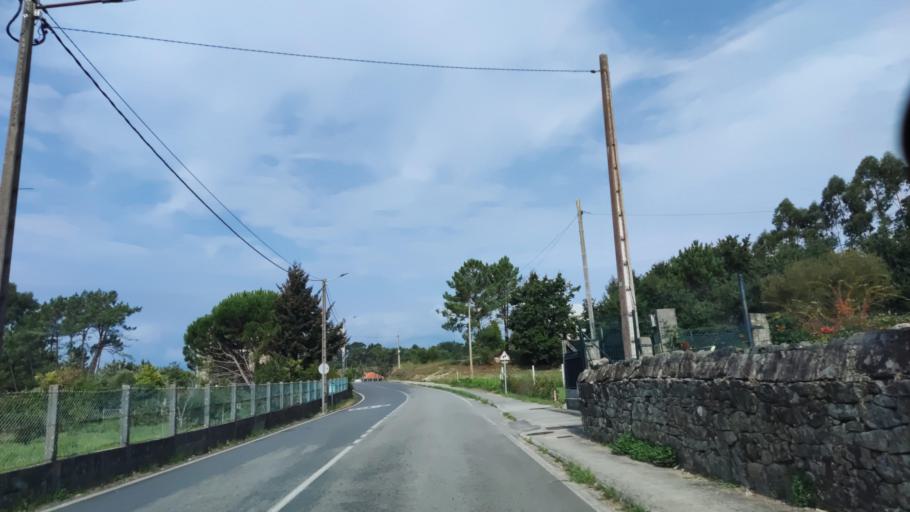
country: ES
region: Galicia
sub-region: Provincia da Coruna
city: Rianxo
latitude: 42.6472
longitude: -8.7992
